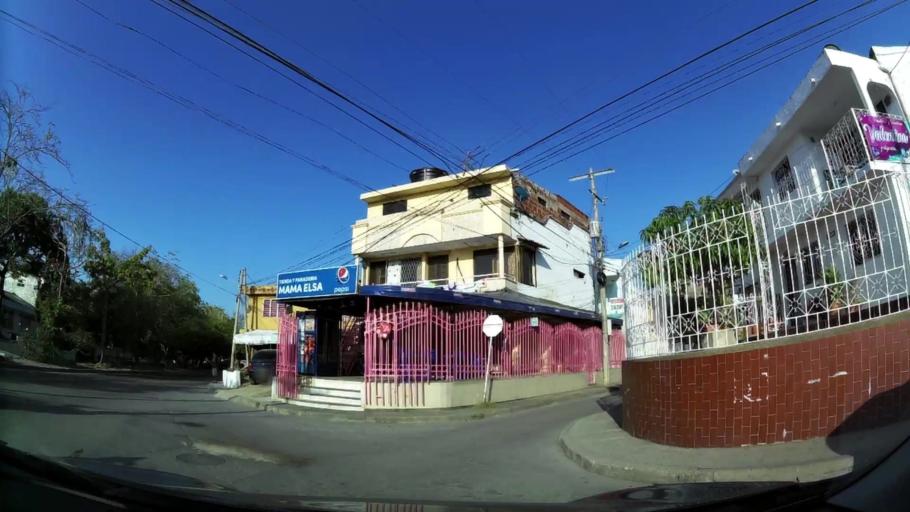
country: CO
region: Bolivar
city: Cartagena
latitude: 10.3808
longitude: -75.4816
